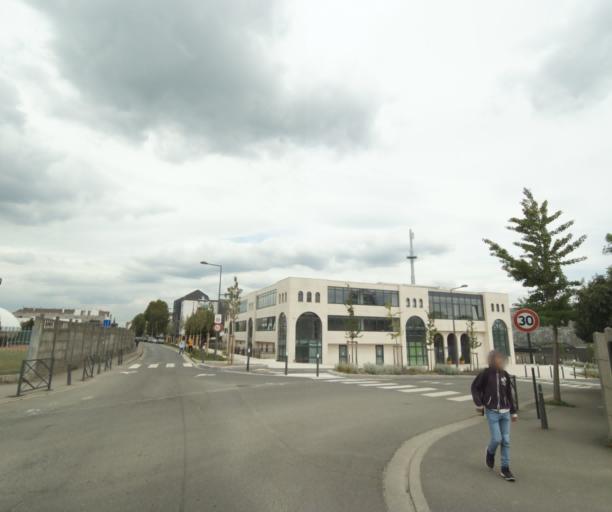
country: FR
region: Ile-de-France
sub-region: Departement des Yvelines
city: Les Mureaux
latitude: 48.9855
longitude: 1.9101
